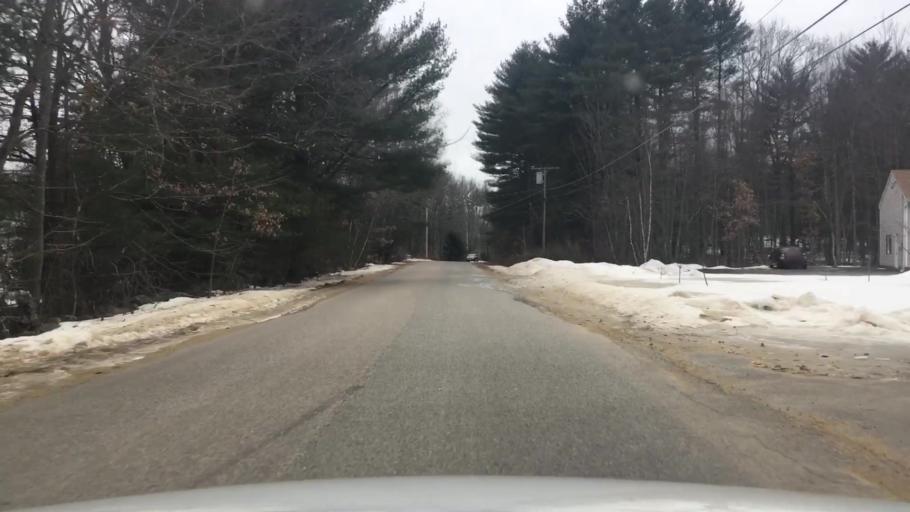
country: US
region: New Hampshire
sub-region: Strafford County
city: Rochester
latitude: 43.3628
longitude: -70.9700
